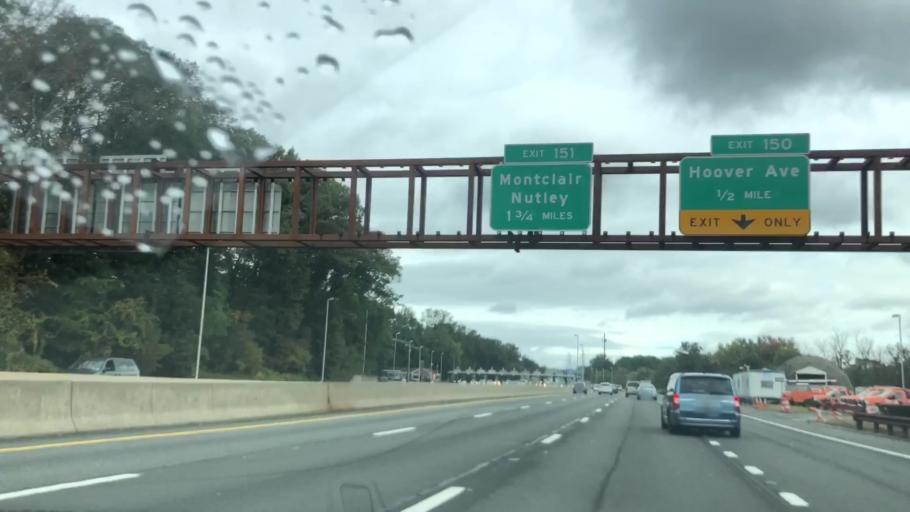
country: US
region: New Jersey
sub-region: Essex County
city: Bloomfield
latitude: 40.8021
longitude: -74.1860
